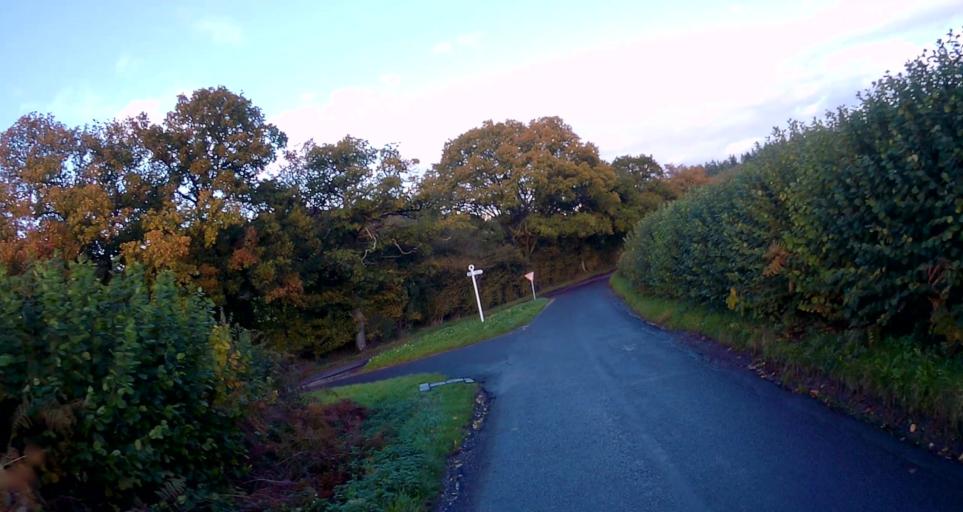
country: GB
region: England
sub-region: Hampshire
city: Basingstoke
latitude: 51.1903
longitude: -1.0768
